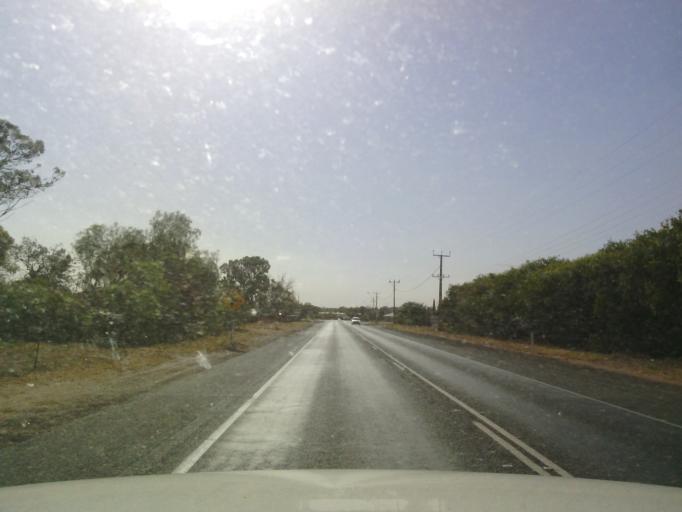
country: AU
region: South Australia
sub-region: Berri and Barmera
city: Berri
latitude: -34.2820
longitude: 140.5832
